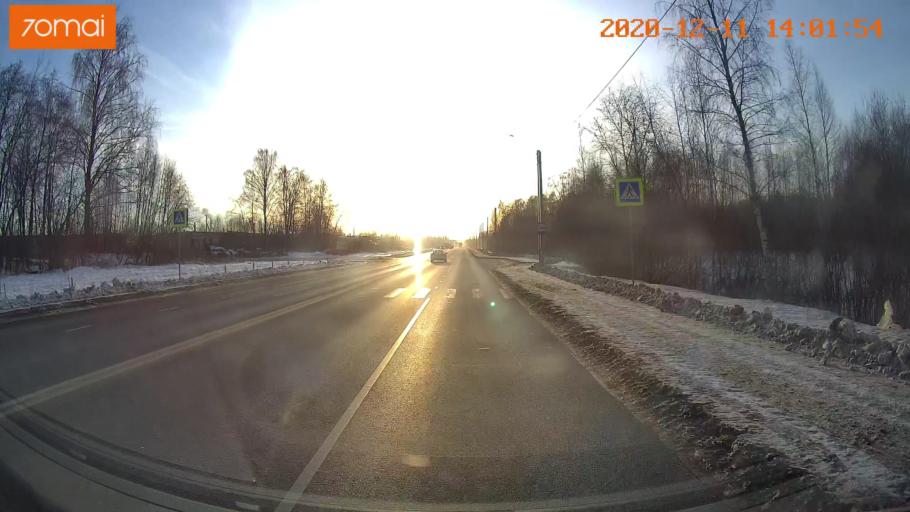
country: RU
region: Kostroma
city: Oktyabr'skiy
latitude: 57.7790
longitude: 41.0322
